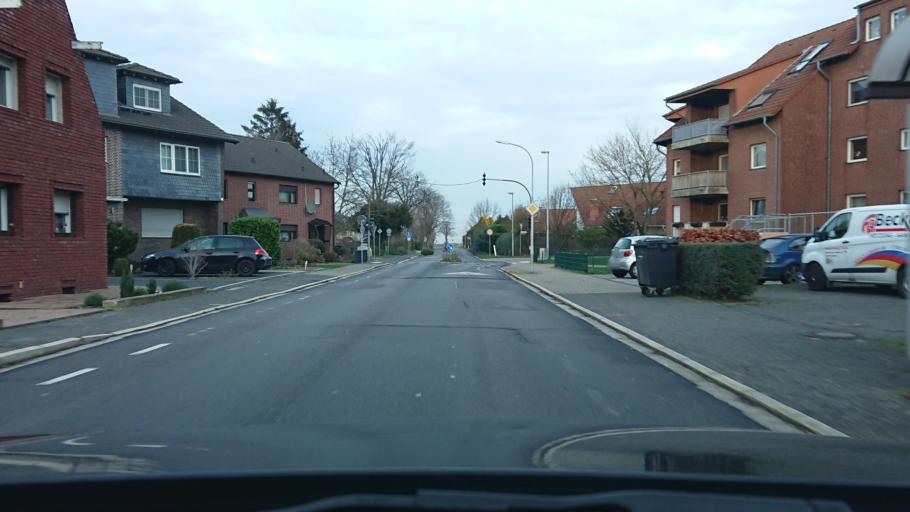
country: DE
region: North Rhine-Westphalia
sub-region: Regierungsbezirk Koln
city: Pulheim
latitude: 50.9942
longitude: 6.7410
